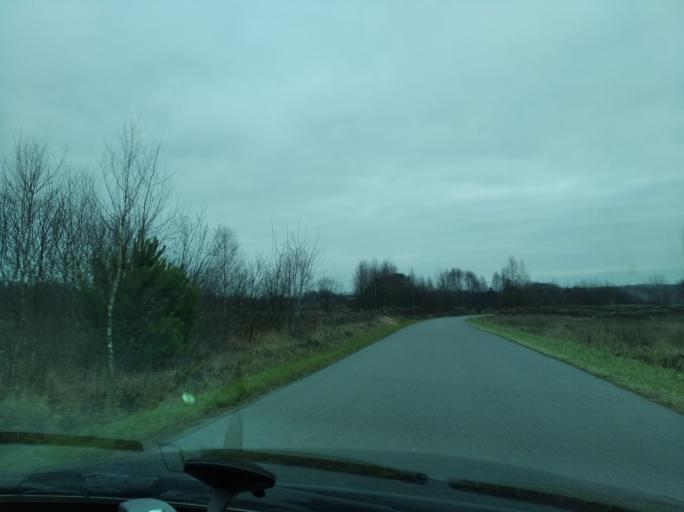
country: PL
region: Subcarpathian Voivodeship
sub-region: Powiat lancucki
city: Brzoza Stadnicka
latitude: 50.2018
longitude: 22.2792
